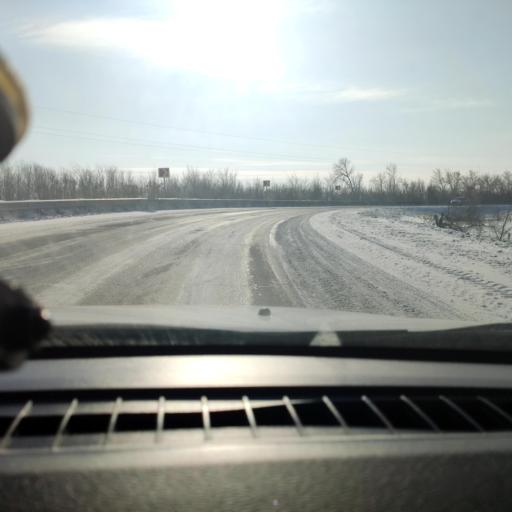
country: RU
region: Samara
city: Smyshlyayevka
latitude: 53.1553
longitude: 50.4565
